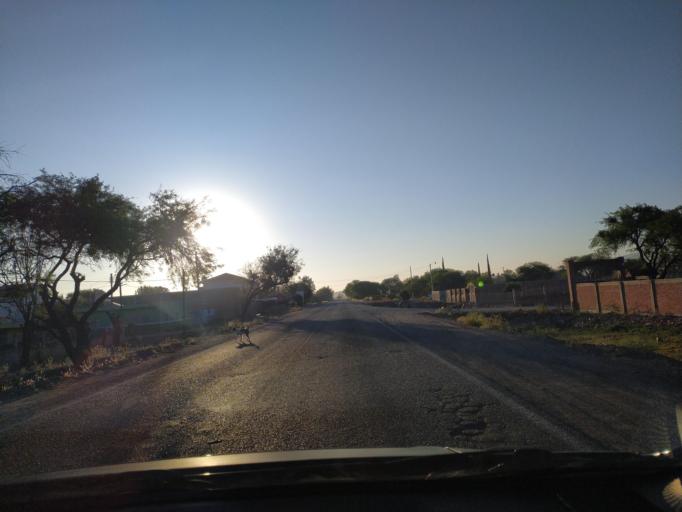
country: MX
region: Guanajuato
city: Ciudad Manuel Doblado
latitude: 20.7405
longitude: -101.8824
